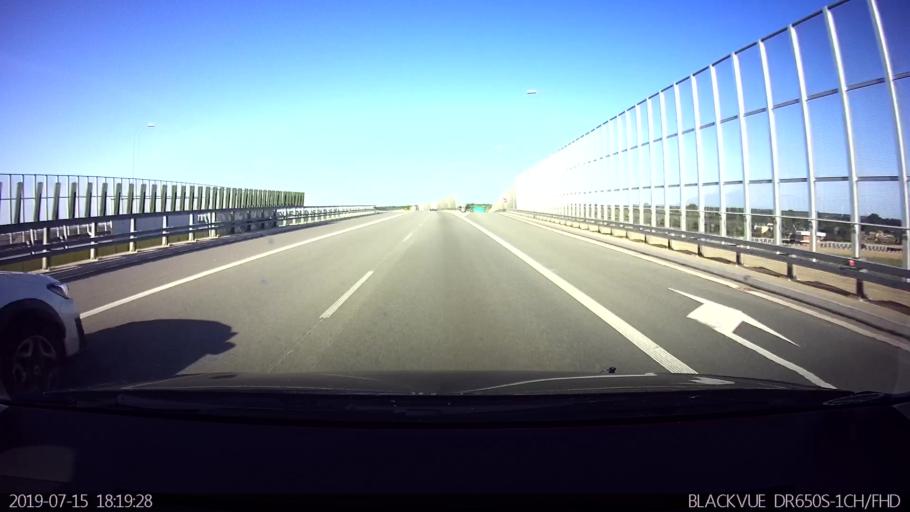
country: PL
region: Lodz Voivodeship
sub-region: Powiat laski
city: Sedziejowice
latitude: 51.5590
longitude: 19.0210
